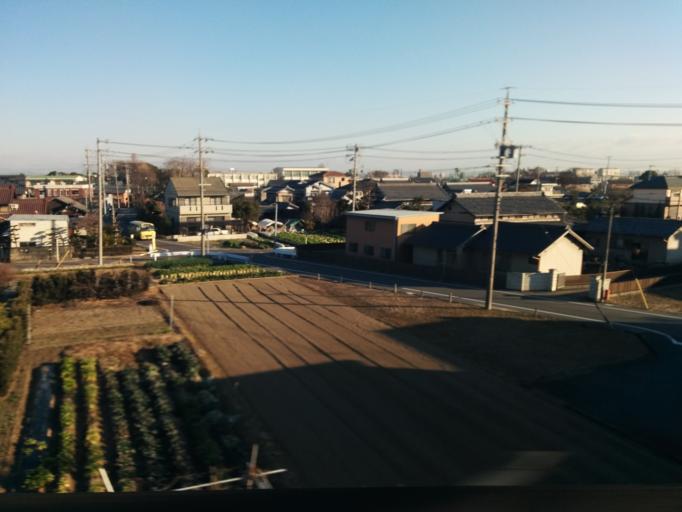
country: JP
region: Aichi
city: Inazawa
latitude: 35.2374
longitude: 136.7849
